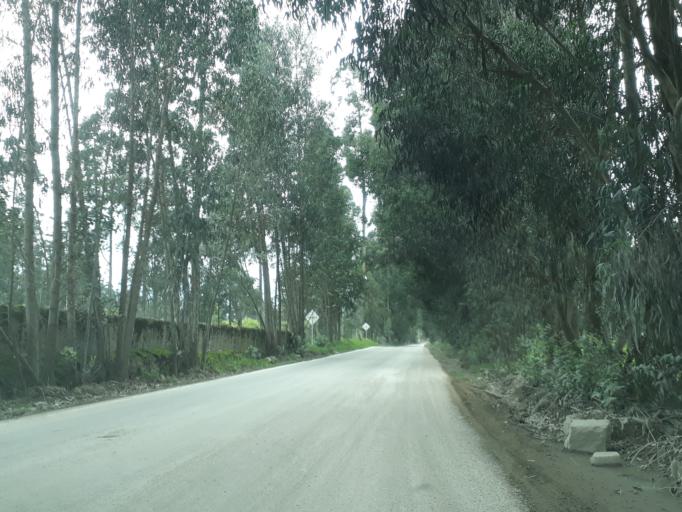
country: CO
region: Cundinamarca
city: Lenguazaque
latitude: 5.3223
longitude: -73.7446
